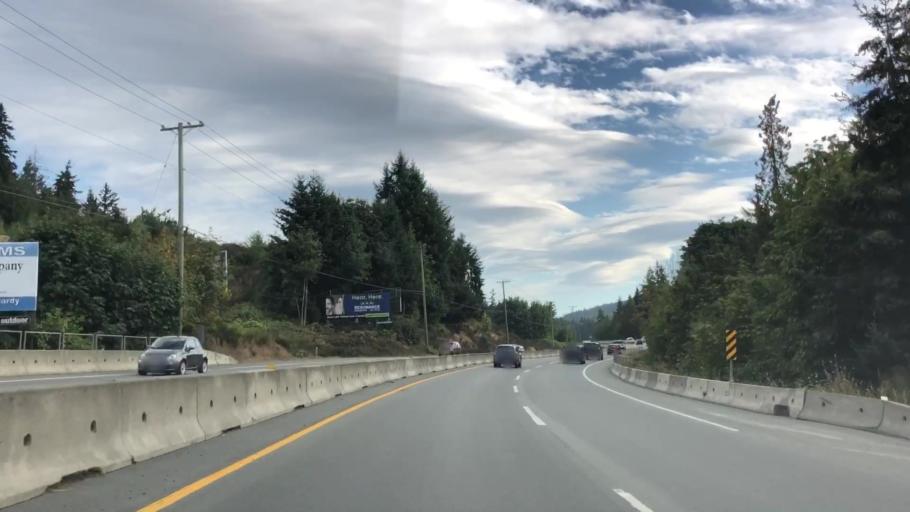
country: CA
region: British Columbia
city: Duncan
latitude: 48.7146
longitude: -123.6097
